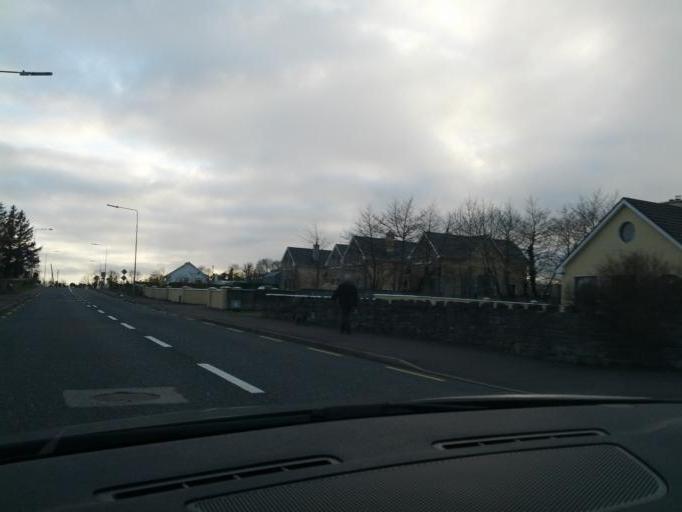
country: IE
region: Connaught
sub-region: Sligo
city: Ballymote
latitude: 54.1330
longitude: -8.5627
